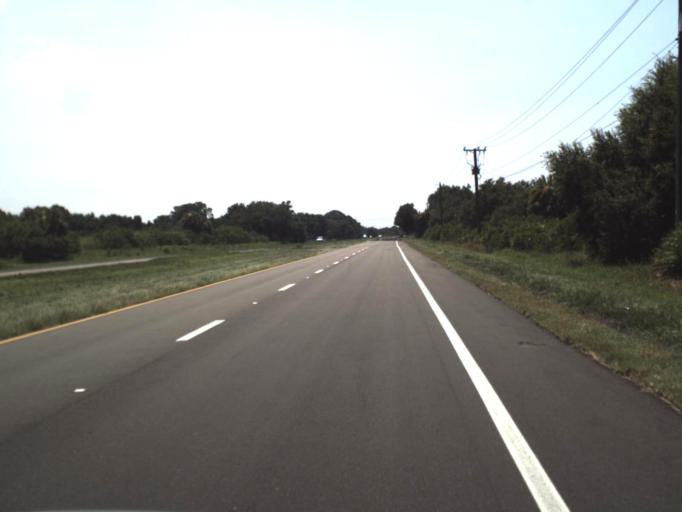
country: US
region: Florida
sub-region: Hillsborough County
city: Ruskin
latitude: 27.6567
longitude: -82.5070
